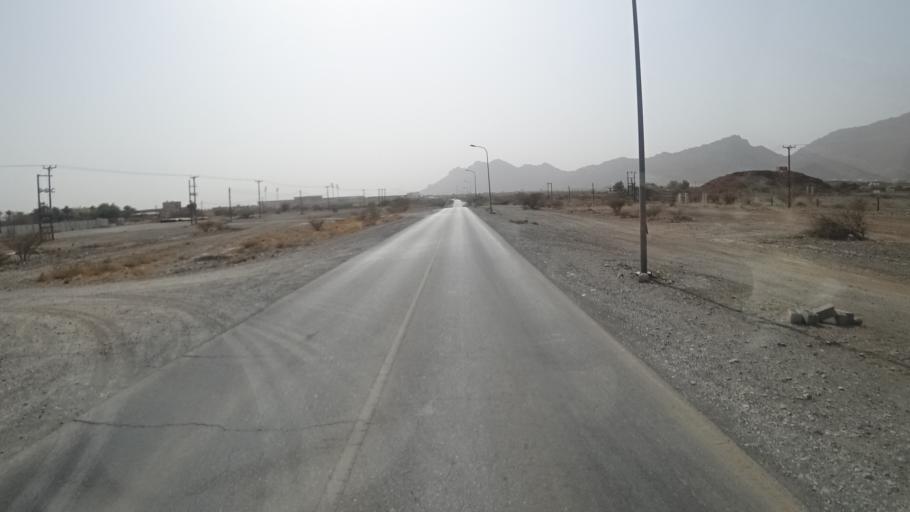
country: OM
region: Muhafazat ad Dakhiliyah
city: Nizwa
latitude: 22.9126
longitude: 57.6007
